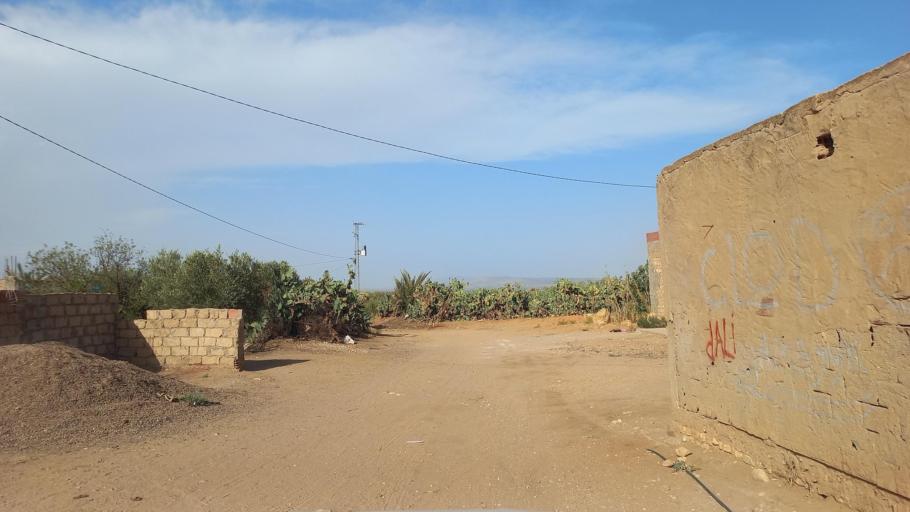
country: TN
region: Al Qasrayn
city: Kasserine
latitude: 35.2091
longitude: 8.9719
